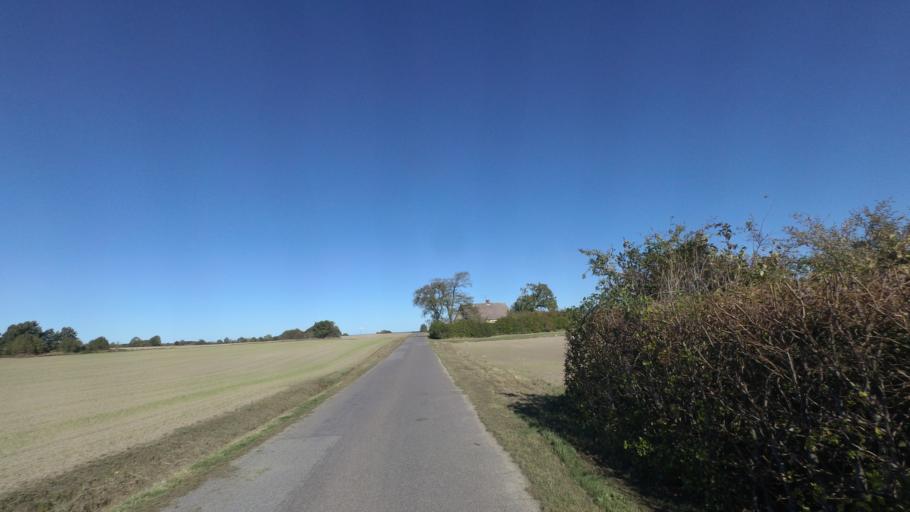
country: DK
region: Capital Region
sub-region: Bornholm Kommune
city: Nexo
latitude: 55.1164
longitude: 15.0440
